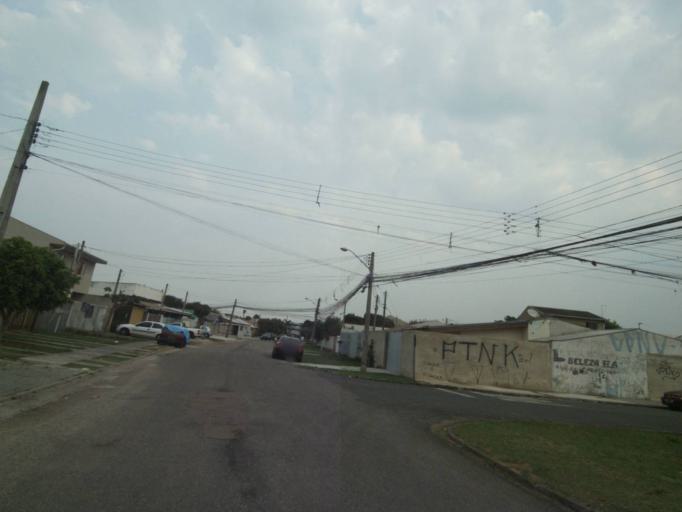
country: BR
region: Parana
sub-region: Sao Jose Dos Pinhais
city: Sao Jose dos Pinhais
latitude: -25.5334
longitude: -49.2510
